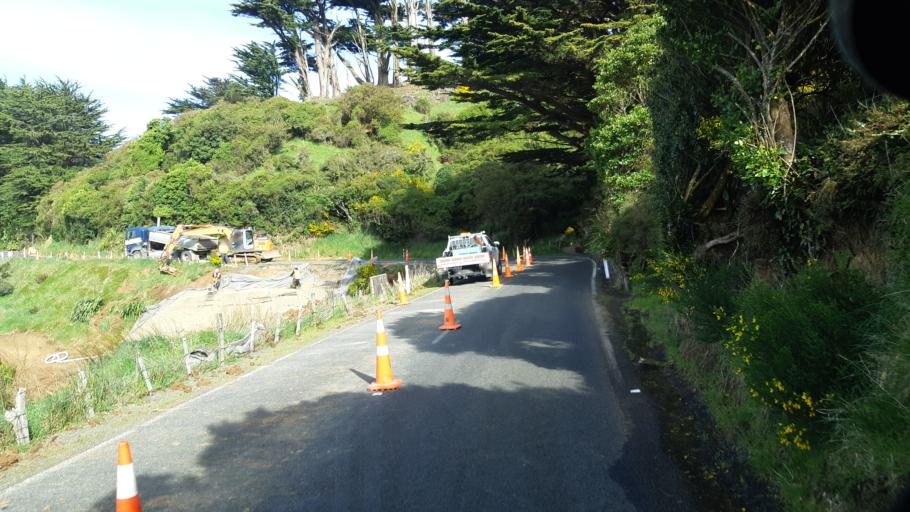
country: NZ
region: Otago
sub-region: Dunedin City
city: Portobello
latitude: -45.8770
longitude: 170.6315
